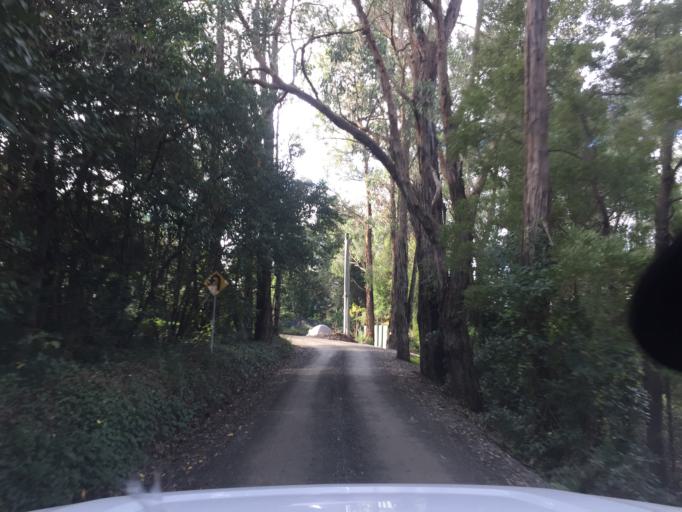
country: AU
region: Victoria
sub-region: Yarra Ranges
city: Mount Evelyn
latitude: -37.7933
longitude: 145.3796
